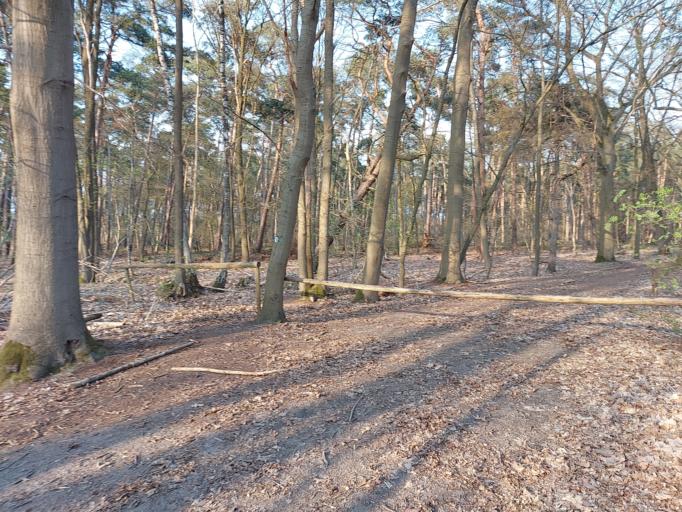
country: BE
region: Flanders
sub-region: Provincie Antwerpen
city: Kasterlee
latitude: 51.2207
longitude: 4.9835
